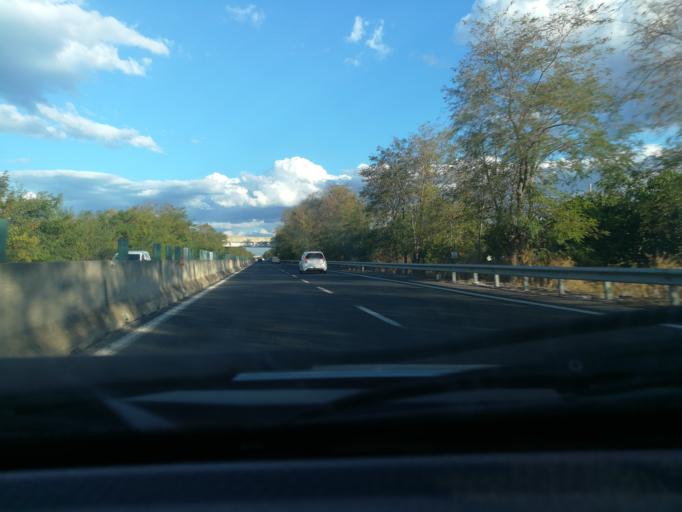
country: IT
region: Apulia
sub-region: Provincia di Bari
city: Mola di Bari
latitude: 41.0417
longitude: 17.1145
